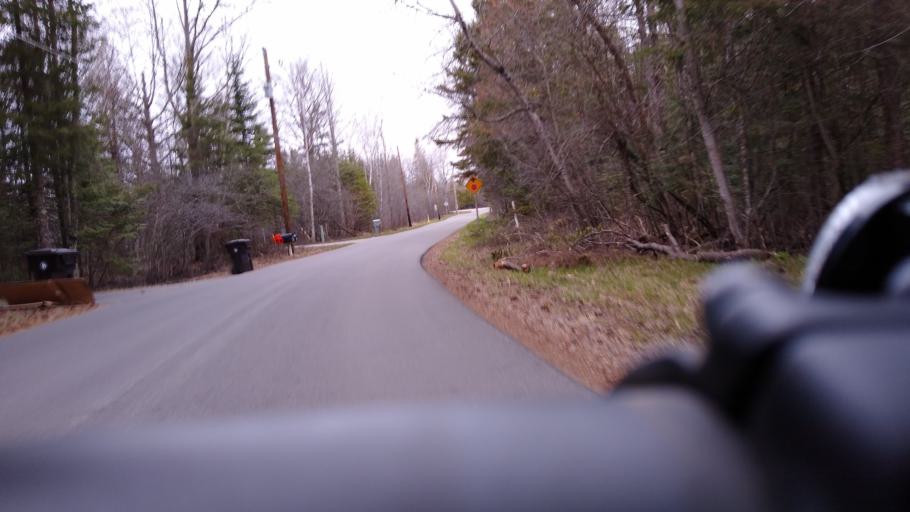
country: US
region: Michigan
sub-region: Delta County
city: Escanaba
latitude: 45.7010
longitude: -87.0987
